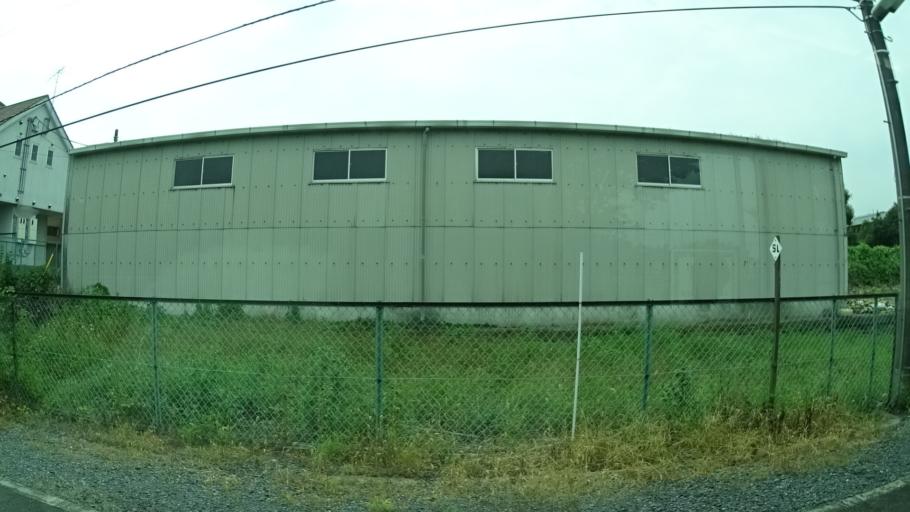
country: JP
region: Tochigi
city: Mooka
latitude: 36.3760
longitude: 139.9717
